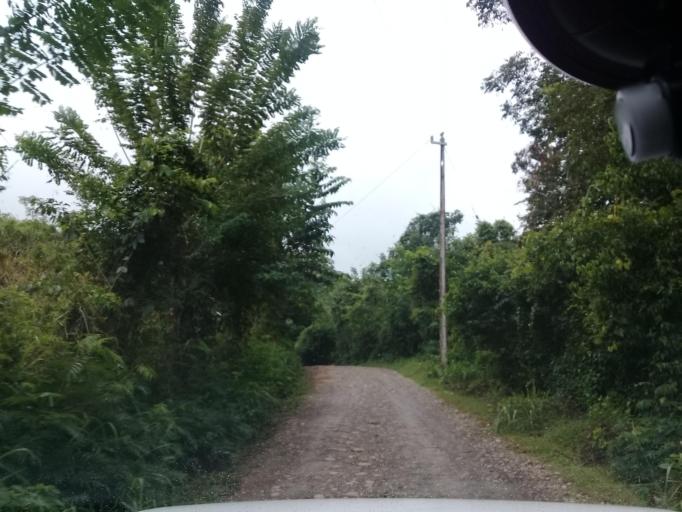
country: MX
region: Veracruz
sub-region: Chalma
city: San Pedro Coyutla
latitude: 21.2410
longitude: -98.4218
